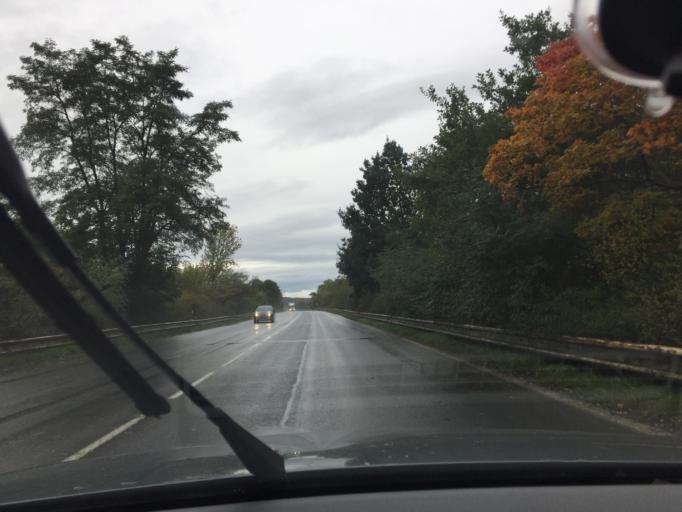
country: CZ
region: Central Bohemia
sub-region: Okres Melnik
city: Veltrusy
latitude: 50.2765
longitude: 14.3183
